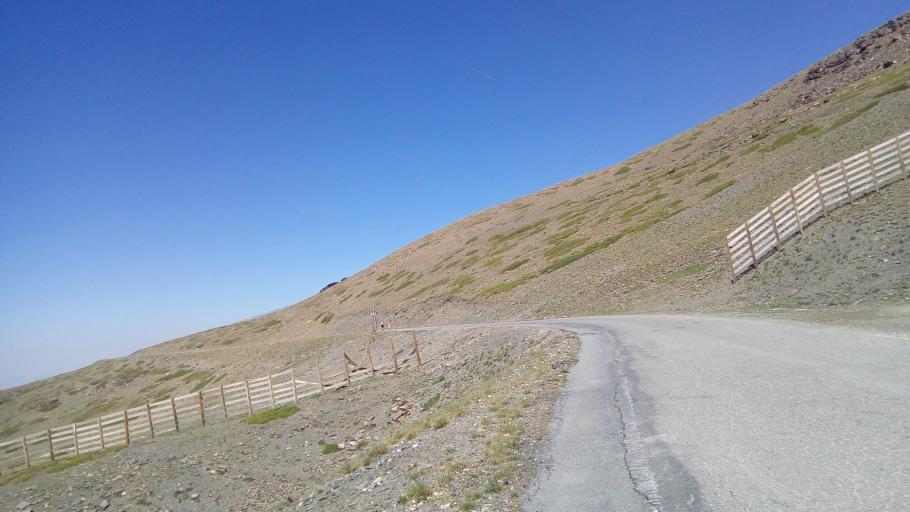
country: ES
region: Andalusia
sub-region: Provincia de Granada
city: Guejar-Sierra
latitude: 37.0769
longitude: -3.3845
